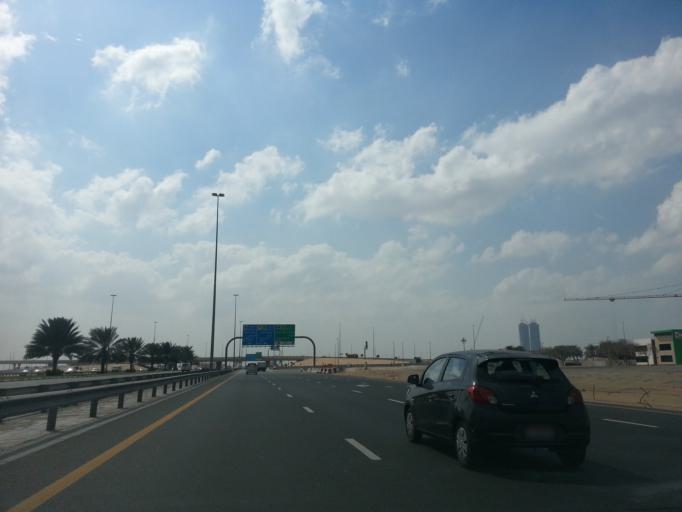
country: AE
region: Ash Shariqah
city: Sharjah
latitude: 25.2129
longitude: 55.3134
